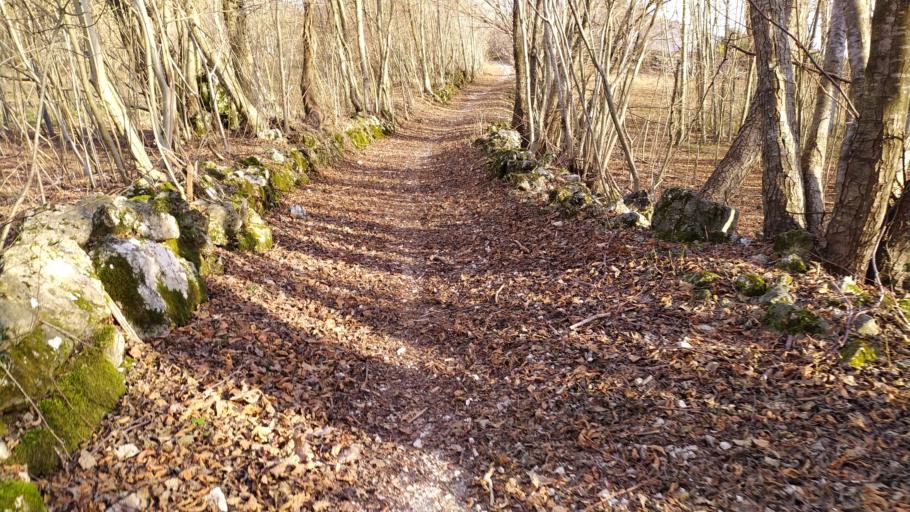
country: IT
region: Veneto
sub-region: Provincia di Vicenza
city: Velo d'Astico
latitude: 45.7681
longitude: 11.3549
